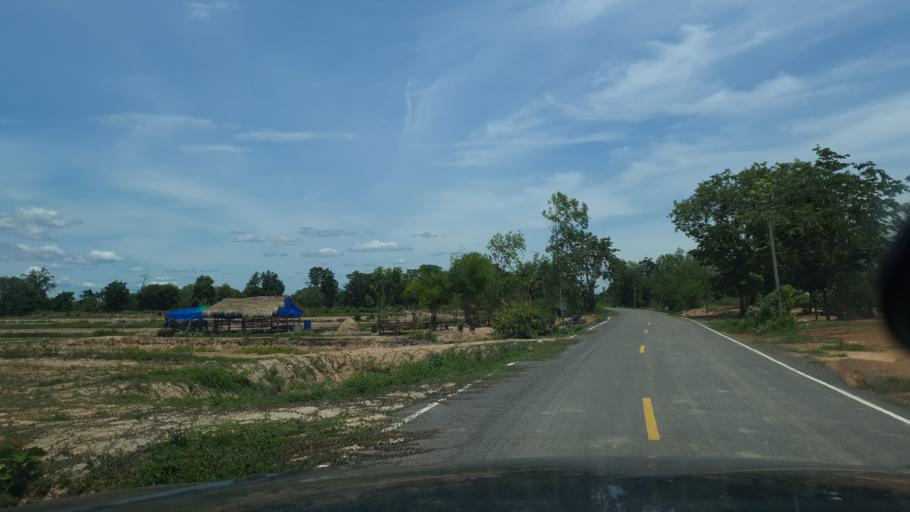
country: TH
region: Sukhothai
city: Ban Na
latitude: 17.1505
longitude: 99.6632
